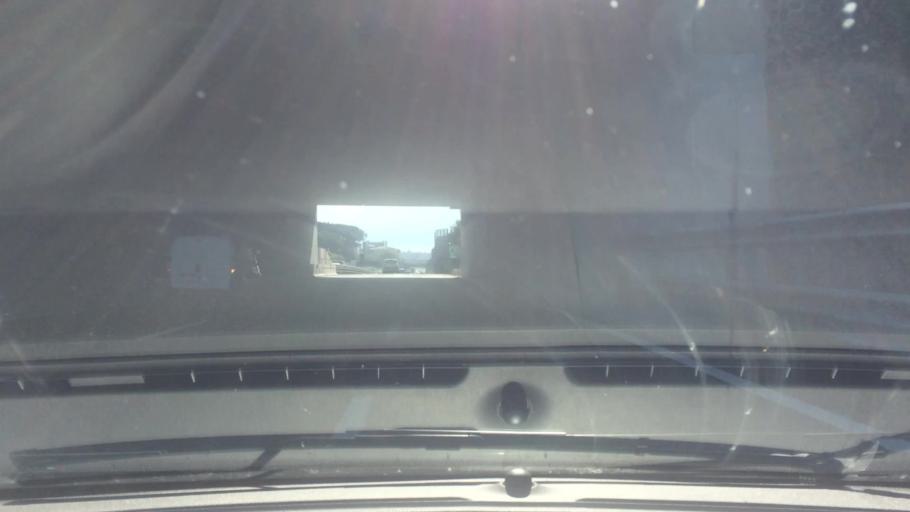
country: IT
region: Campania
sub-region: Provincia di Napoli
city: Ercolano
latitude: 40.7972
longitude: 14.3726
